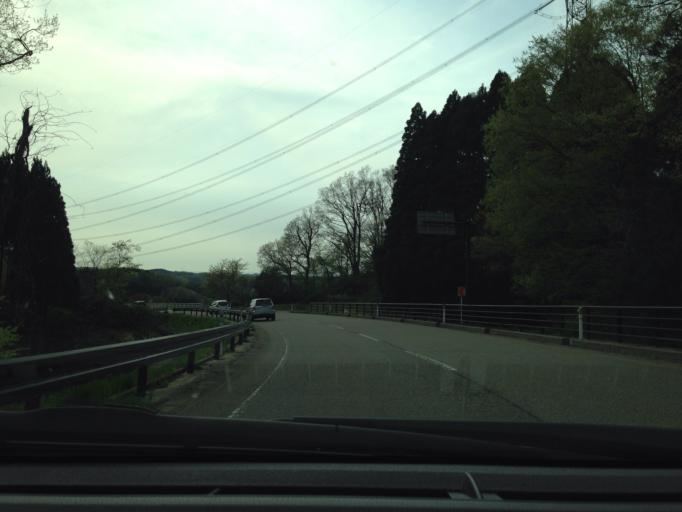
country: JP
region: Toyama
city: Fukumitsu
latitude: 36.5694
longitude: 136.7911
